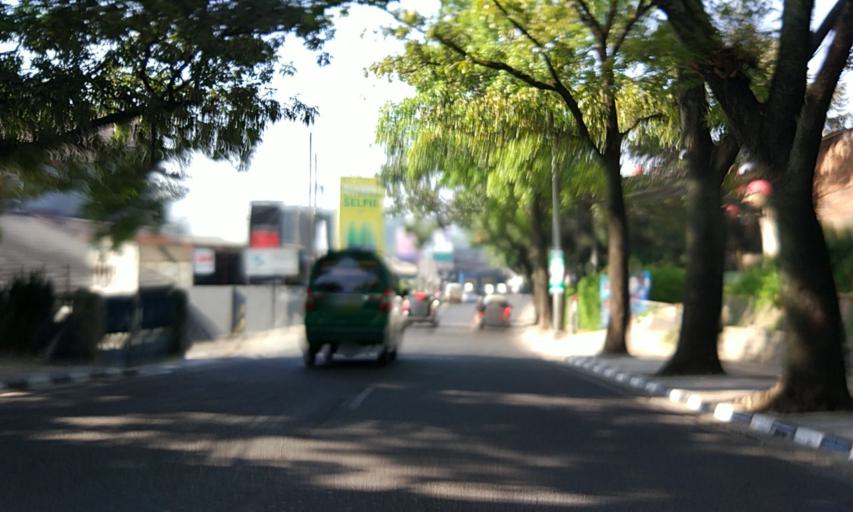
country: ID
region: West Java
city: Bandung
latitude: -6.8838
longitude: 107.6039
